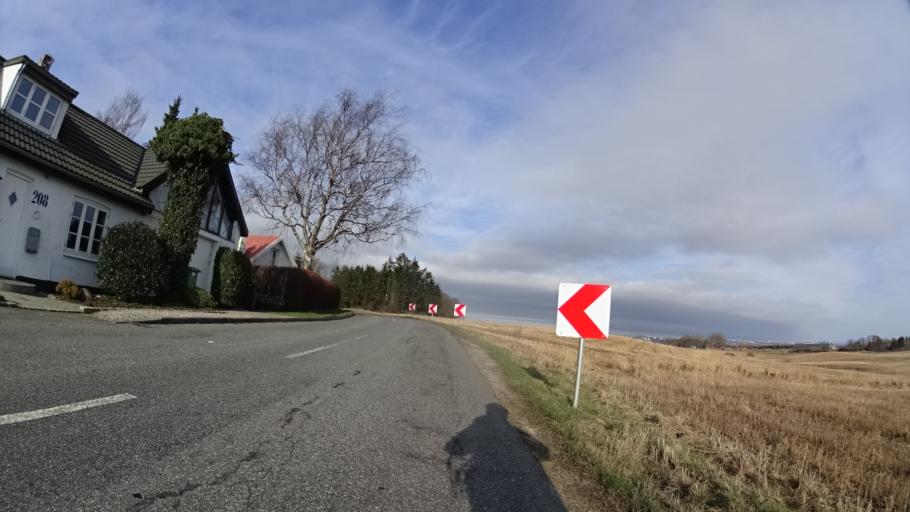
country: DK
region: Central Jutland
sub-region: Arhus Kommune
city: Stavtrup
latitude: 56.1109
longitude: 10.1104
